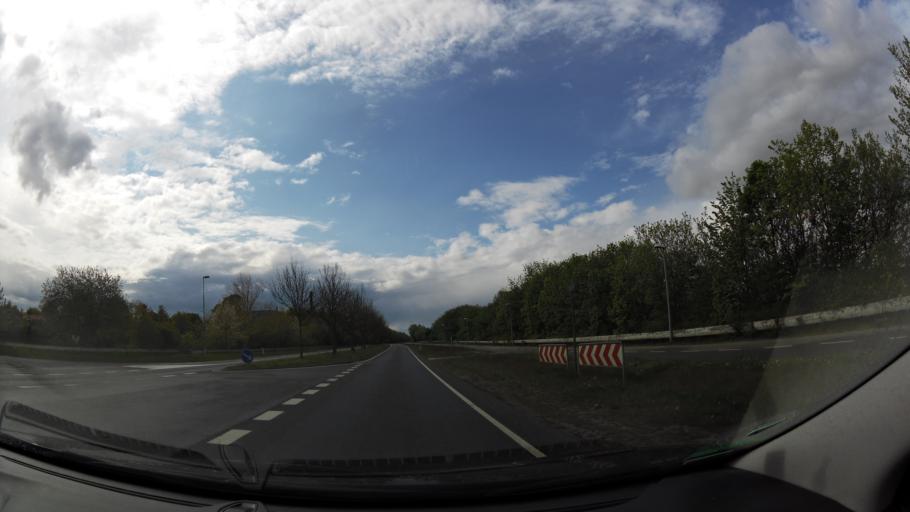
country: DK
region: South Denmark
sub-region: Nyborg Kommune
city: Nyborg
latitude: 55.3122
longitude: 10.7688
